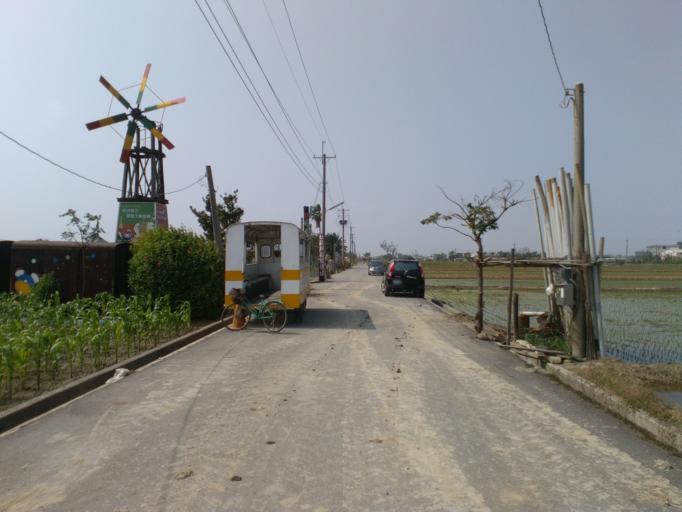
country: TW
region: Taiwan
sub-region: Chiayi
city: Taibao
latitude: 23.5629
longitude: 120.3246
